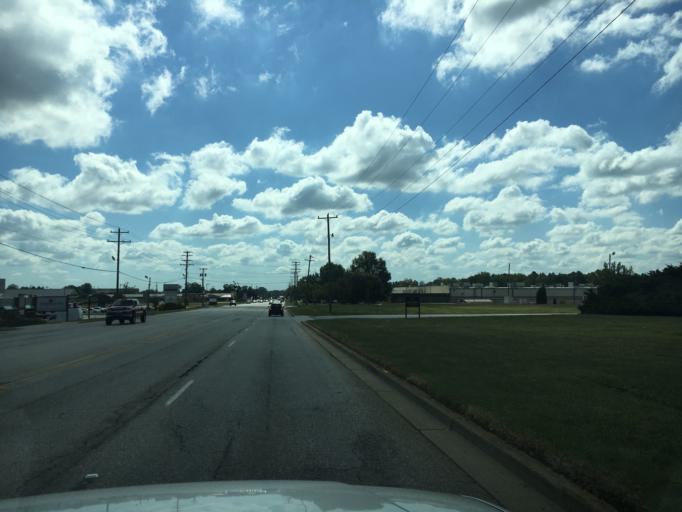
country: US
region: South Carolina
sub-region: Greenville County
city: Greer
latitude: 34.9371
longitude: -82.2551
